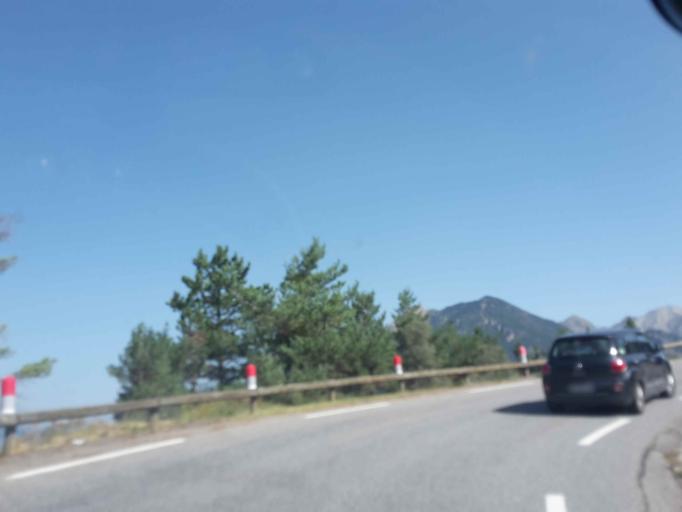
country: FR
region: Provence-Alpes-Cote d'Azur
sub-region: Departement des Hautes-Alpes
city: Guillestre
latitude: 44.6431
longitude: 6.6624
